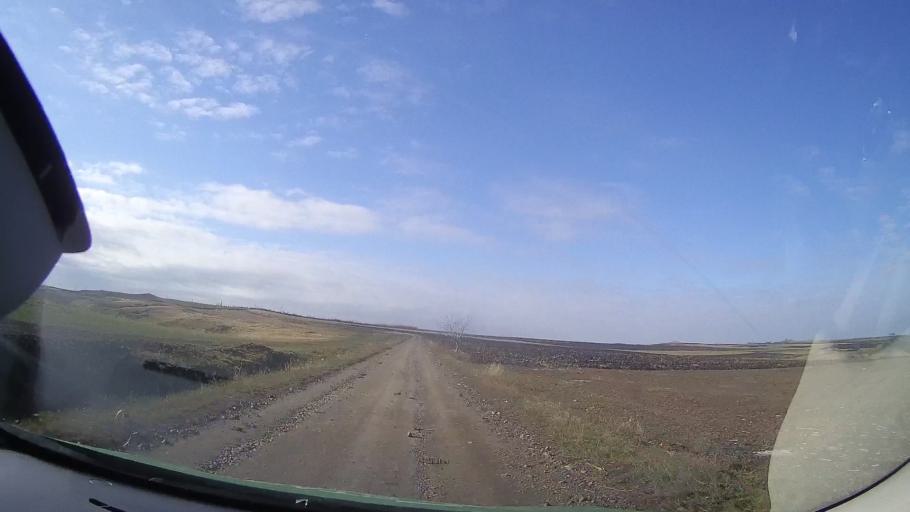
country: RO
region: Mures
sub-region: Comuna Saulia
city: Saulia
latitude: 46.5981
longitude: 24.2255
